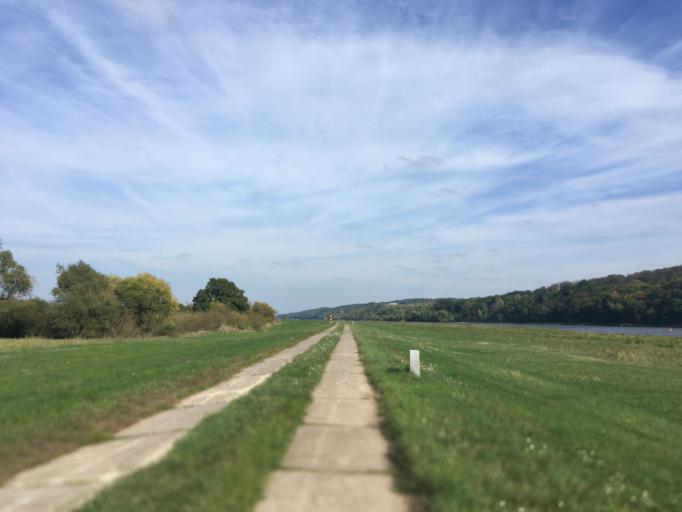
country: DE
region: Brandenburg
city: Meyenburg
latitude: 53.0020
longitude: 14.2515
